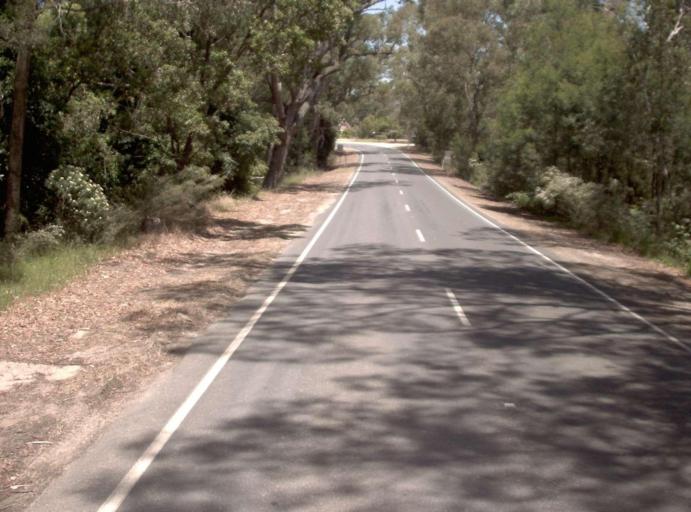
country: AU
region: Victoria
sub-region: East Gippsland
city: Lakes Entrance
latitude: -37.6928
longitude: 147.8374
